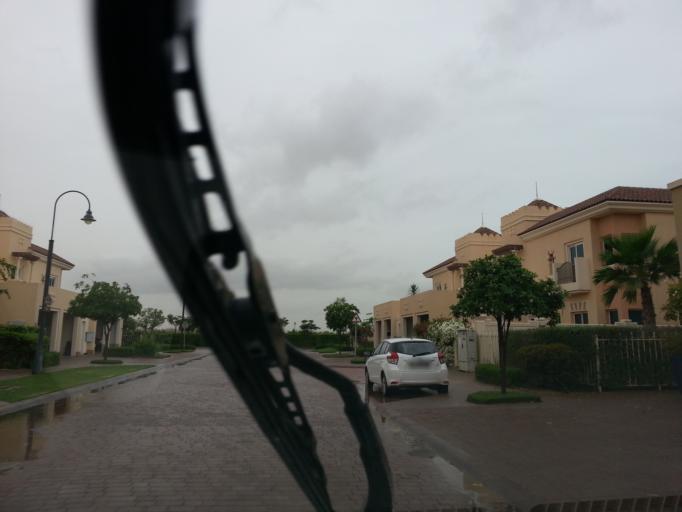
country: AE
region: Dubai
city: Dubai
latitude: 25.0279
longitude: 55.2106
